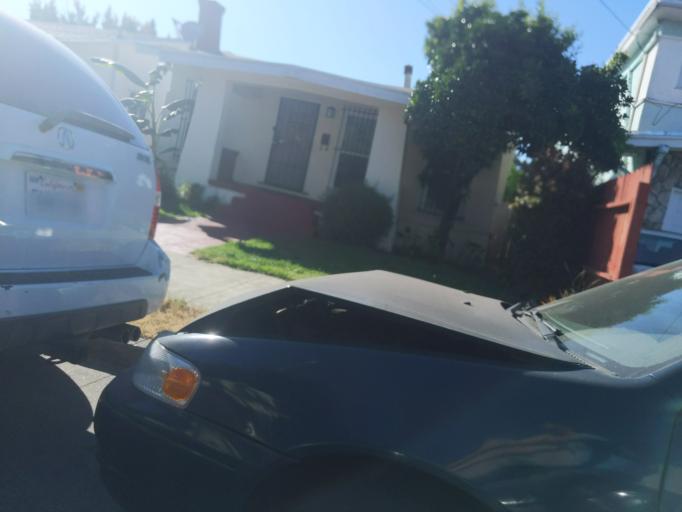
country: US
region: California
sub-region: Alameda County
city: Alameda
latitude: 37.7890
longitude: -122.2088
